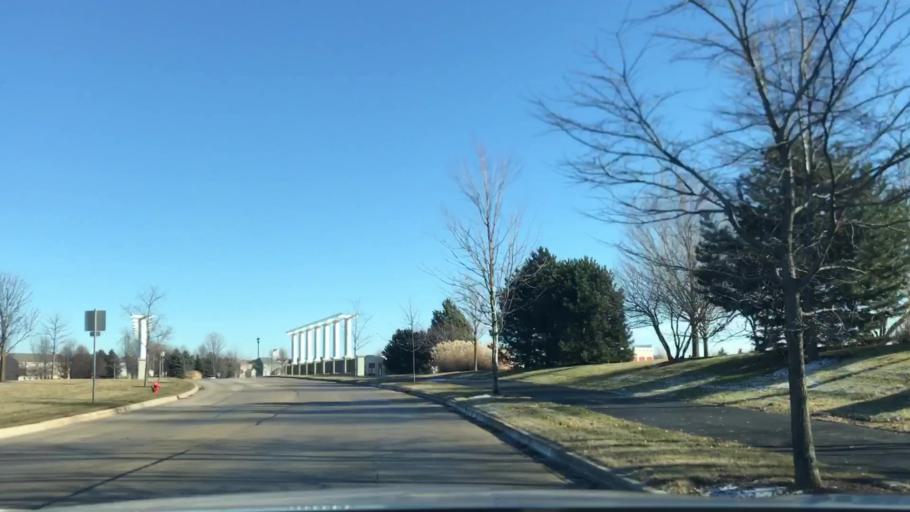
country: US
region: Illinois
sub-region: Kane County
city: Pingree Grove
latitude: 42.0854
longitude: -88.4385
